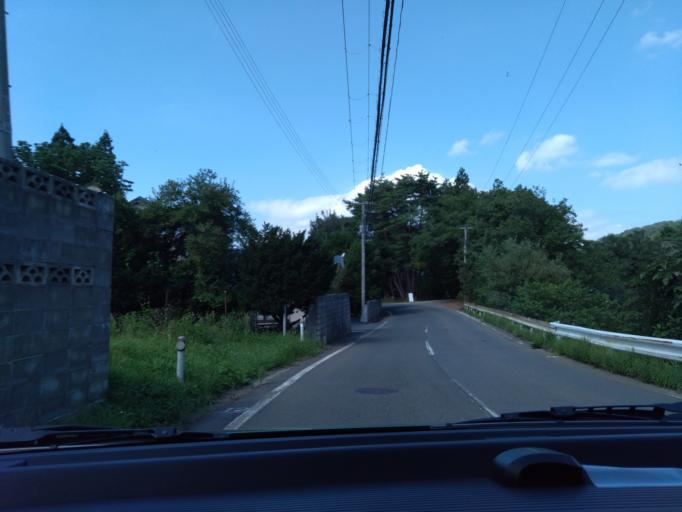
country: JP
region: Iwate
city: Shizukuishi
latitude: 39.6527
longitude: 140.9927
